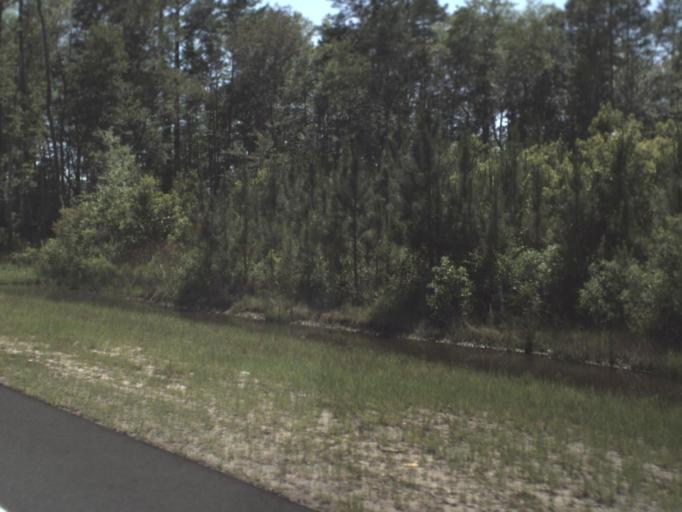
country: US
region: Florida
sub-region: Duval County
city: Baldwin
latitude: 30.3605
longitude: -81.9481
